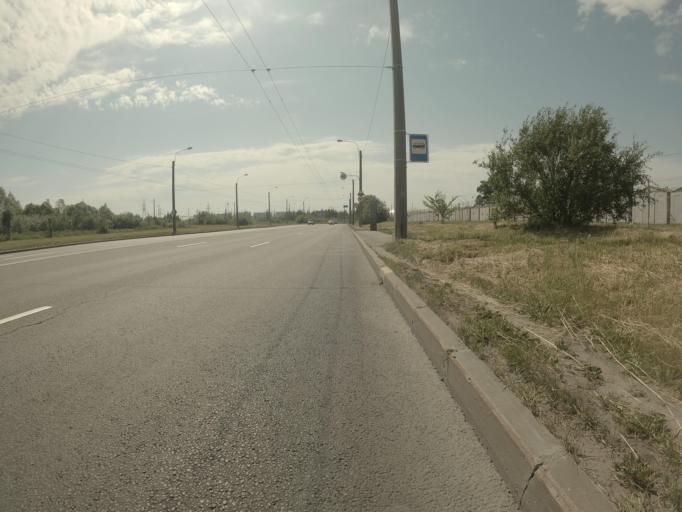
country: RU
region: St.-Petersburg
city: Krasnogvargeisky
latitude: 59.9364
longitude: 30.5034
